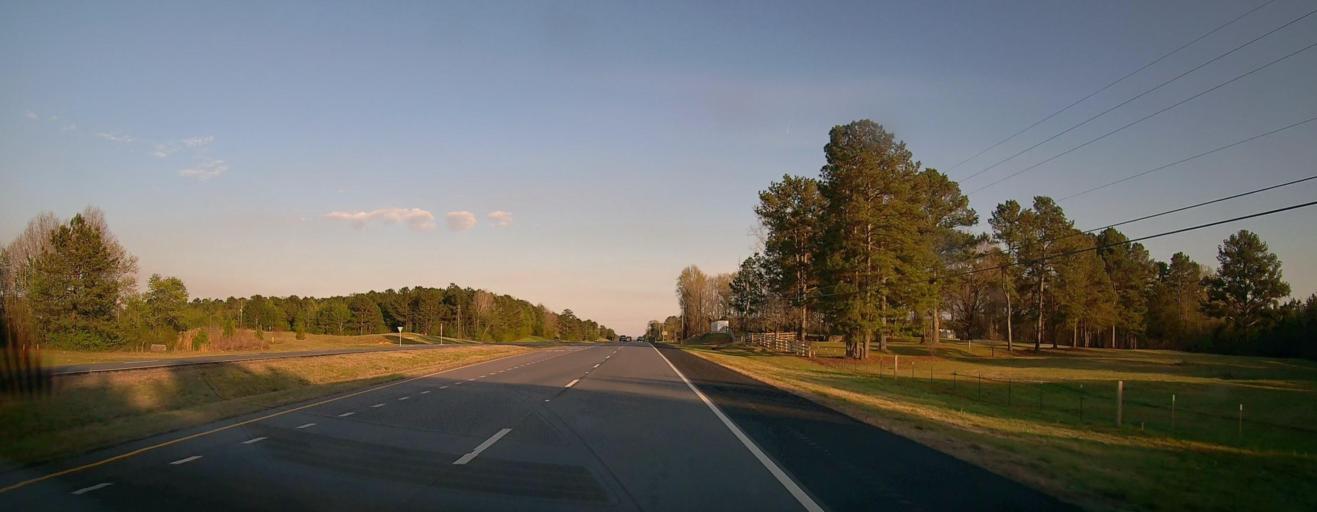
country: US
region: Alabama
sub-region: Shelby County
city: Harpersville
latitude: 33.3188
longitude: -86.3975
